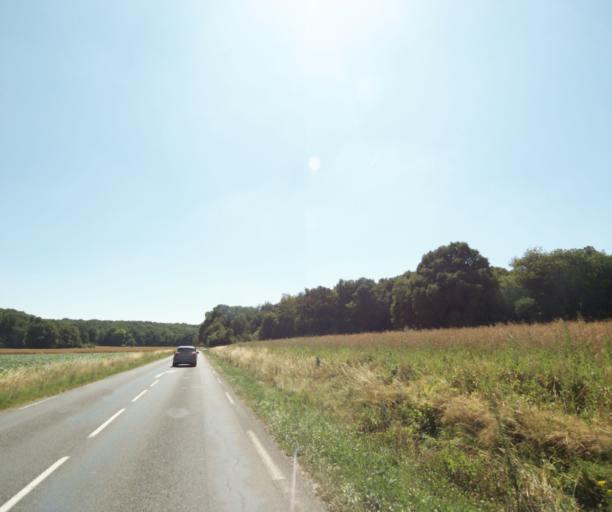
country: FR
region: Ile-de-France
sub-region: Departement de l'Essonne
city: Milly-la-Foret
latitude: 48.3683
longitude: 2.4709
